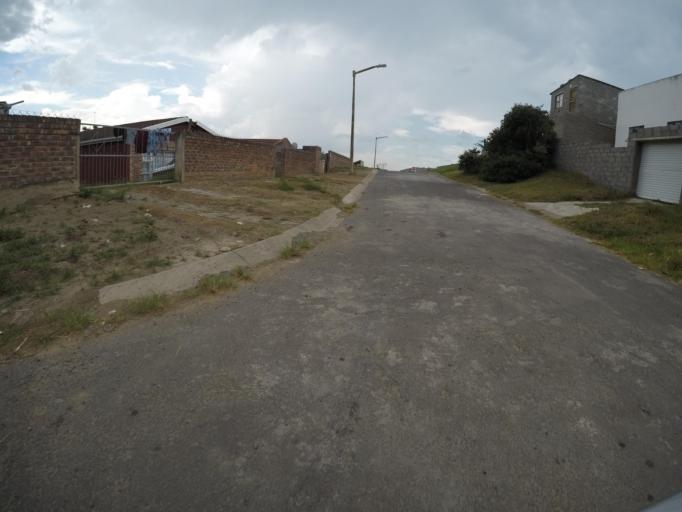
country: ZA
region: Eastern Cape
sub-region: Buffalo City Metropolitan Municipality
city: East London
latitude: -33.0212
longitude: 27.8649
